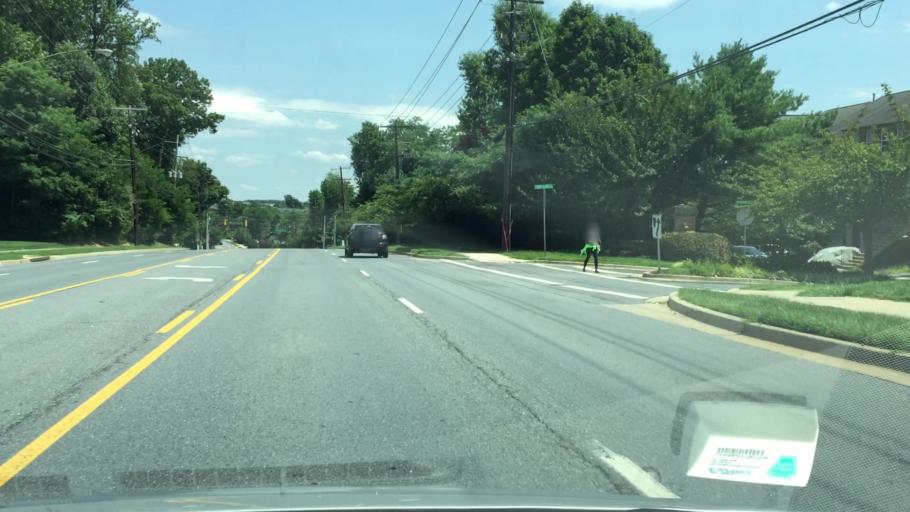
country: US
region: Maryland
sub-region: Montgomery County
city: Leisure World
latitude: 39.0910
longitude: -77.0613
